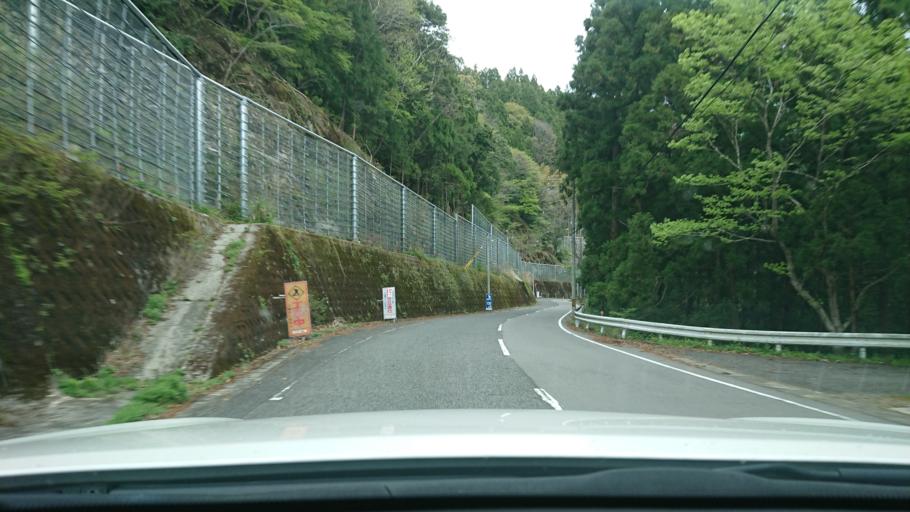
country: JP
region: Tokushima
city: Ishii
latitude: 33.9115
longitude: 134.4208
